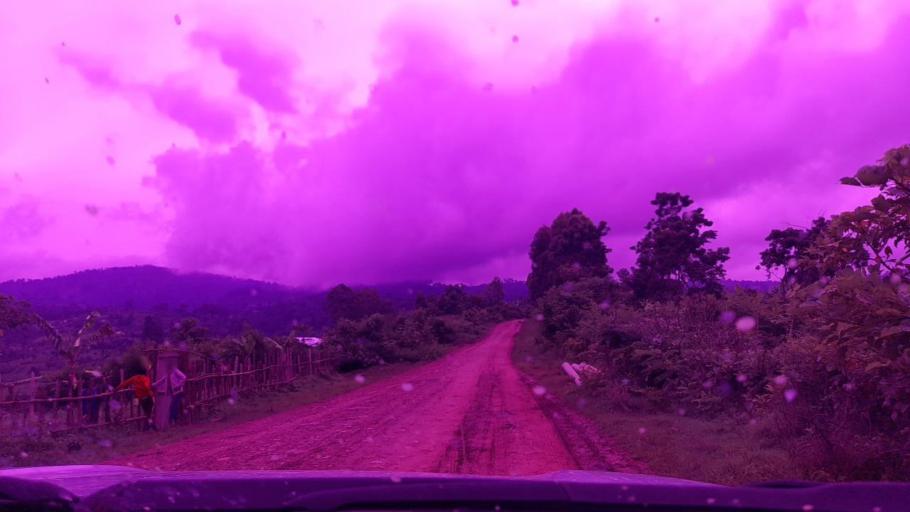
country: ET
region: Southern Nations, Nationalities, and People's Region
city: Bonga
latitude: 7.5527
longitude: 35.8396
